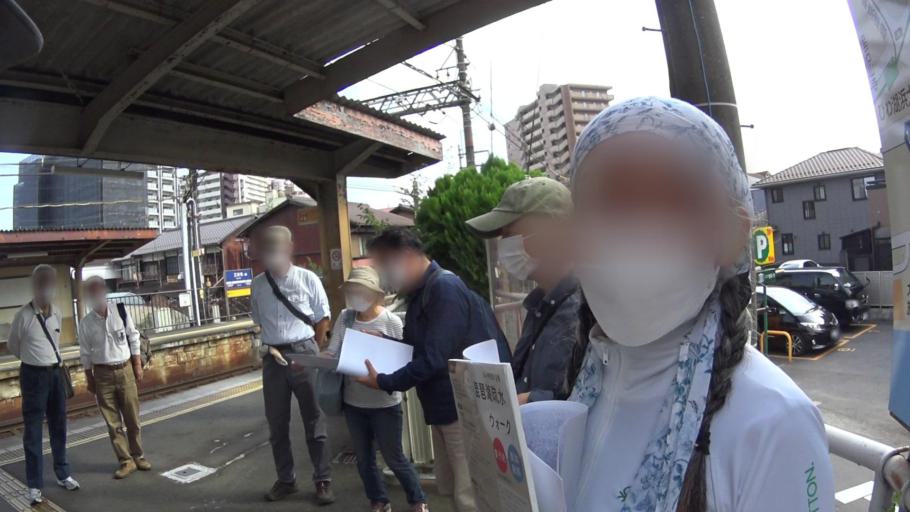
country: JP
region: Osaka
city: Izumiotsu
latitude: 34.5222
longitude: 135.3548
